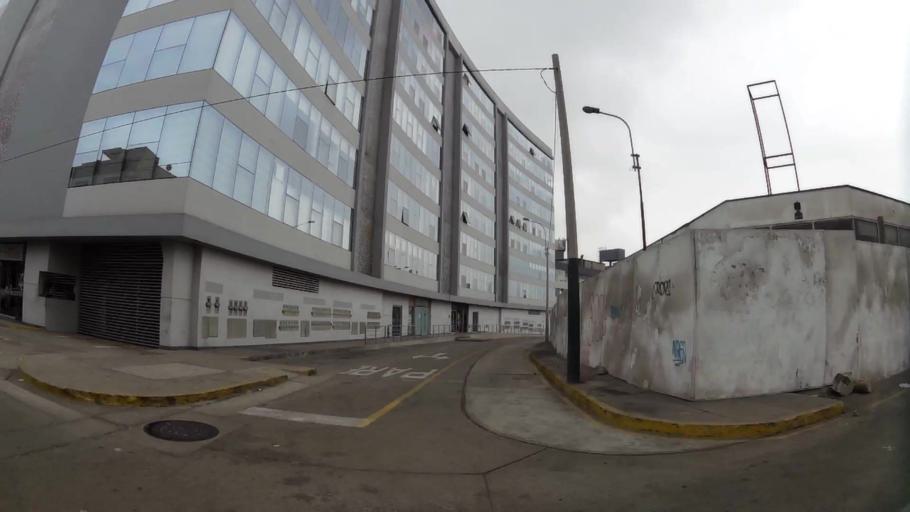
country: PE
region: Lima
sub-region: Lima
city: Surco
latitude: -12.1265
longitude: -76.9878
